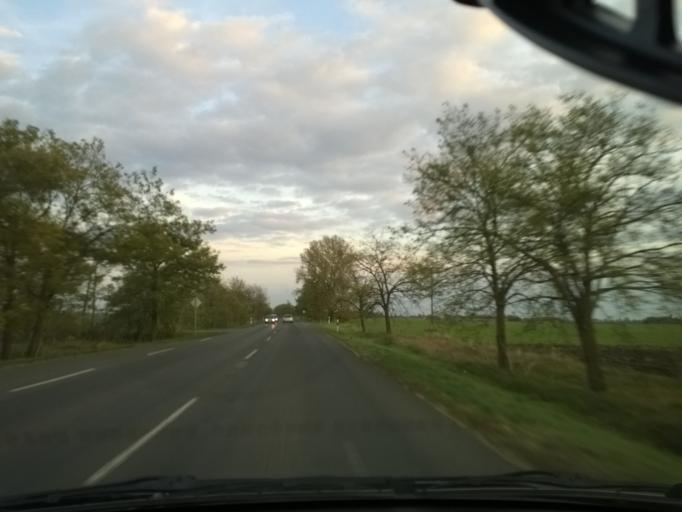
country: HU
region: Bacs-Kiskun
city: Palmonostora
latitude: 46.6916
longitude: 19.9381
